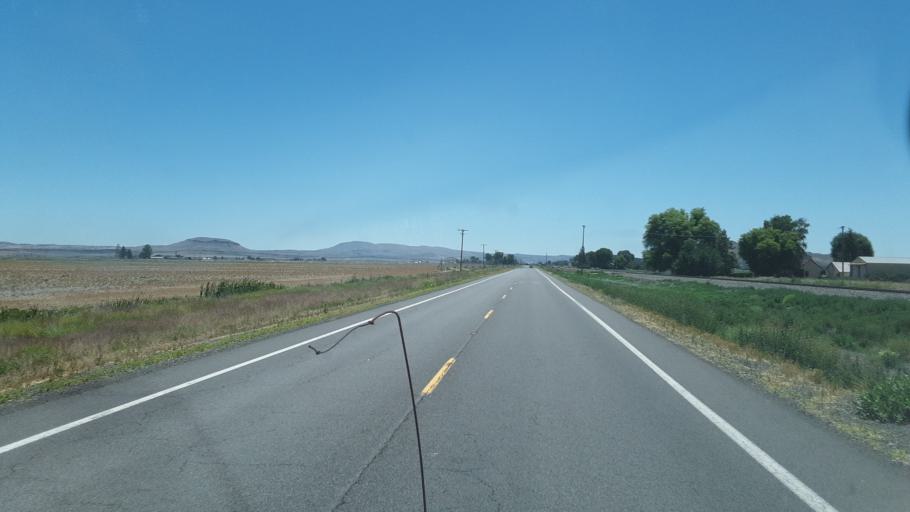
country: US
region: California
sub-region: Siskiyou County
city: Tulelake
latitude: 41.9195
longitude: -121.4308
